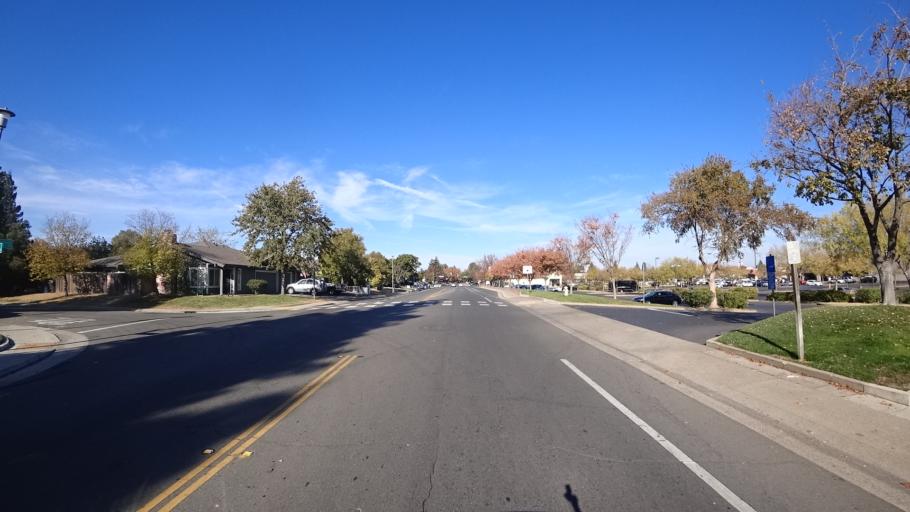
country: US
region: California
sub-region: Sacramento County
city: Antelope
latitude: 38.7055
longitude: -121.3154
